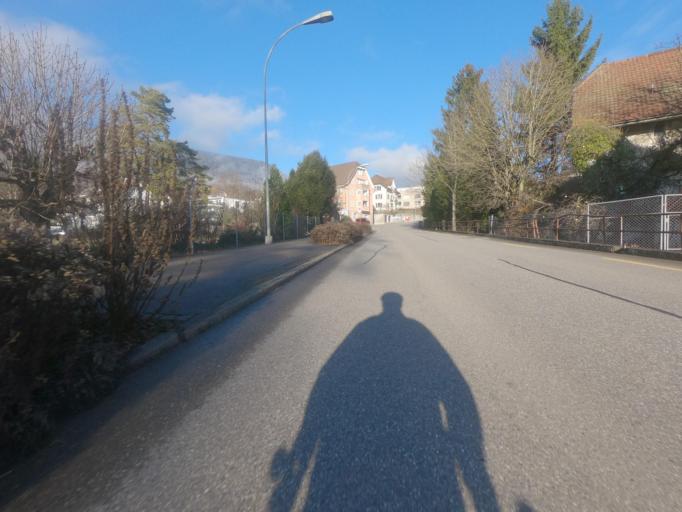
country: CH
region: Solothurn
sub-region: Bezirk Lebern
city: Grenchen
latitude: 47.1914
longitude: 7.3859
